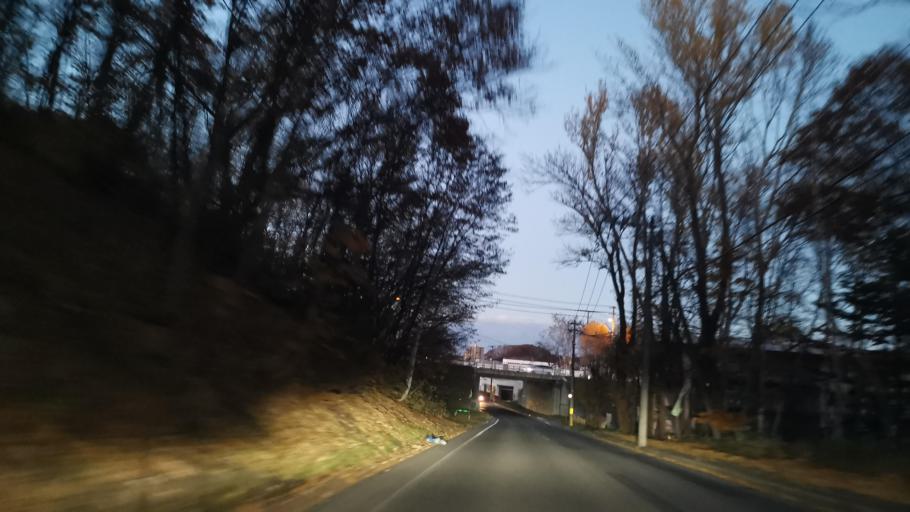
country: JP
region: Hokkaido
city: Sapporo
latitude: 42.9975
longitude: 141.3632
